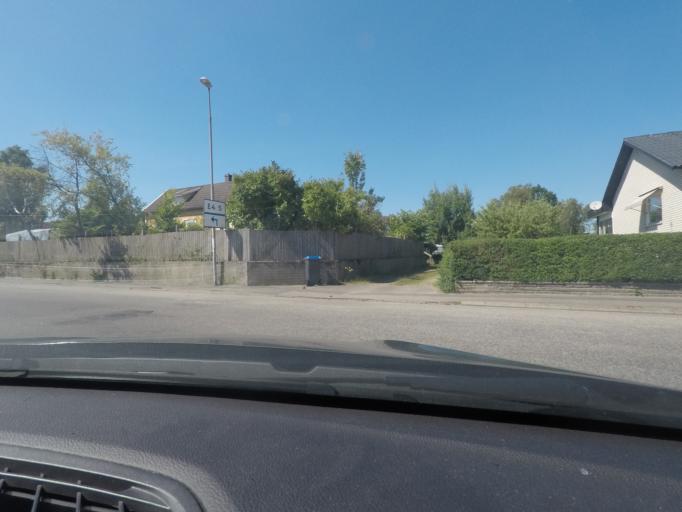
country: SE
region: Kronoberg
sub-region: Markaryds Kommun
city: Markaryd
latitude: 56.4499
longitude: 13.5980
